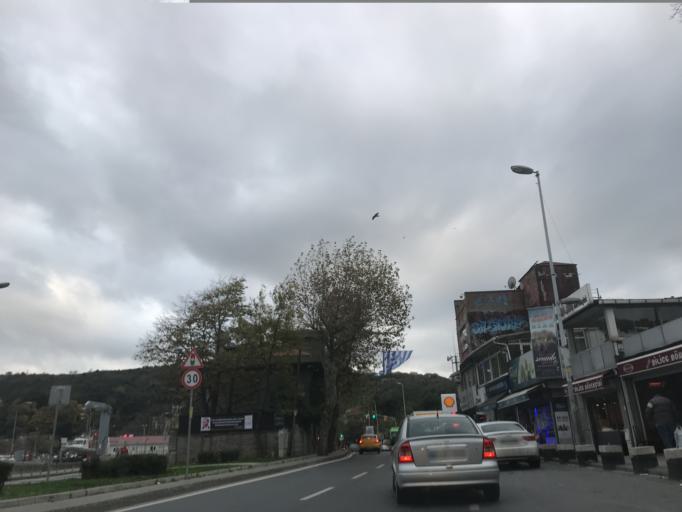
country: TR
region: Istanbul
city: Arikoey
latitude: 41.1571
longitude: 29.0362
